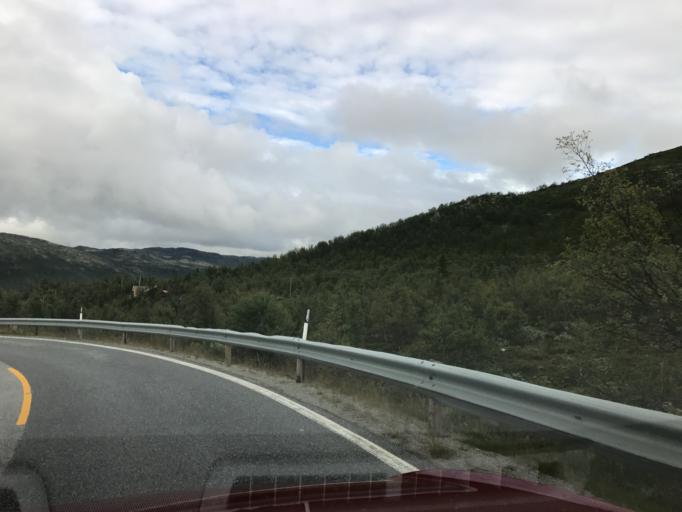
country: NO
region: Buskerud
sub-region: Al
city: Al
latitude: 60.3329
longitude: 8.5000
